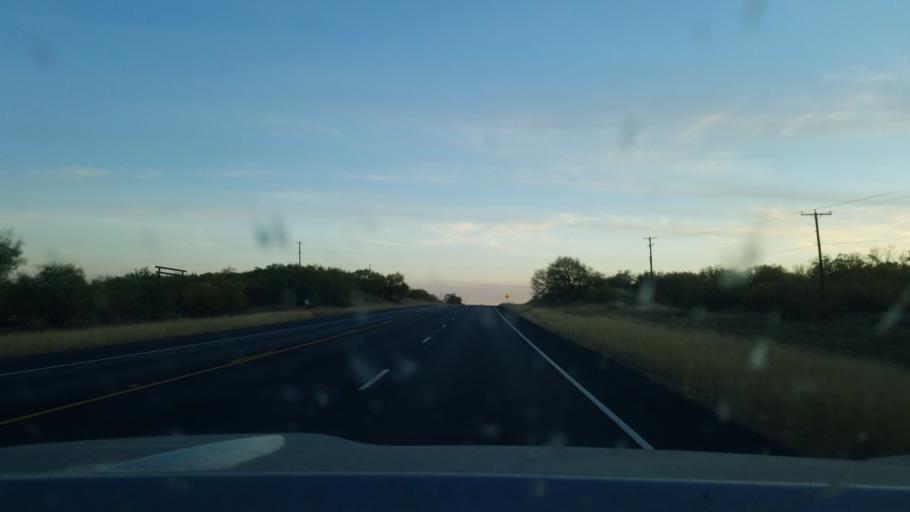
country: US
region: Texas
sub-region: Stephens County
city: Breckenridge
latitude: 32.6835
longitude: -98.9025
